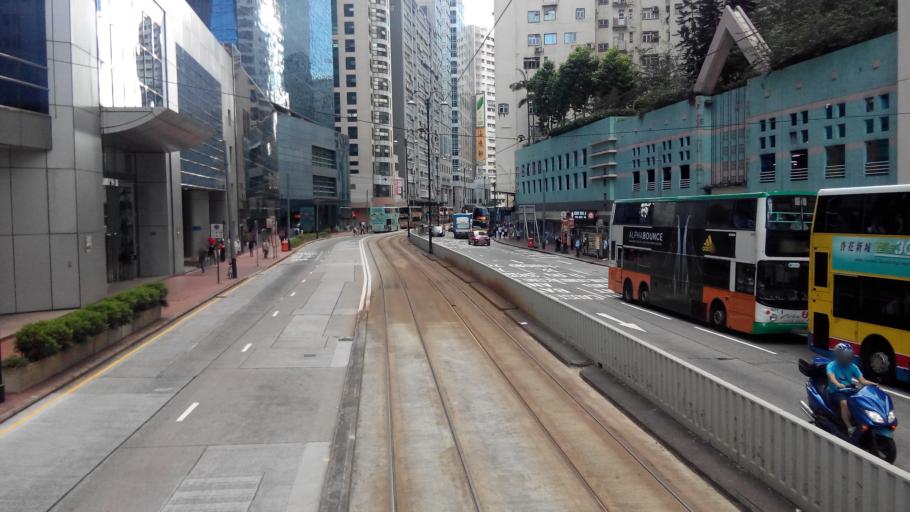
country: HK
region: Kowloon City
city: Kowloon
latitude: 22.2921
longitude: 114.2058
